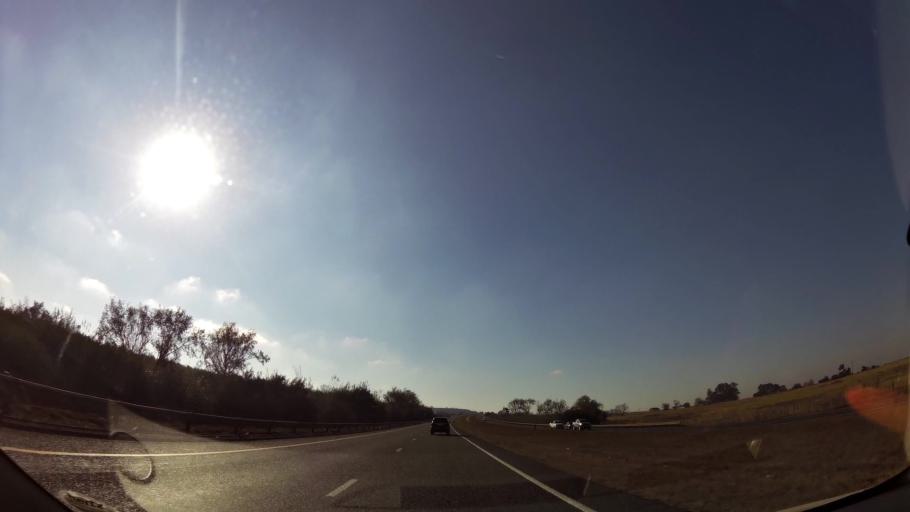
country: ZA
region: Gauteng
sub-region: City of Tshwane Metropolitan Municipality
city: Bronkhorstspruit
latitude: -26.0167
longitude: 28.9485
